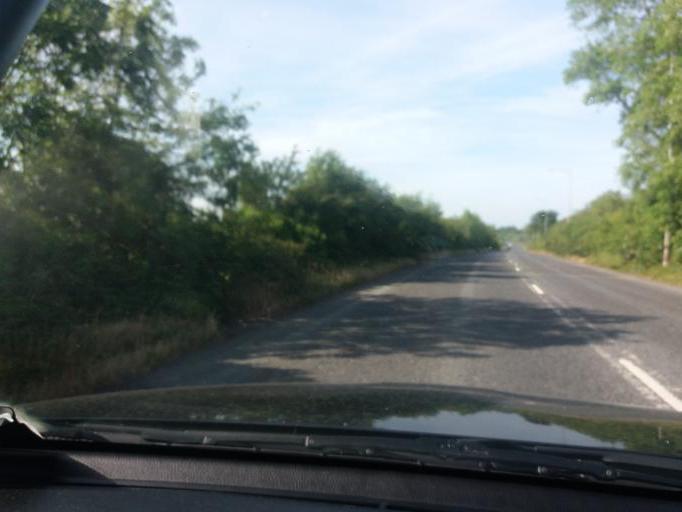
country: IE
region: Leinster
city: Balrothery
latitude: 53.5575
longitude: -6.2113
